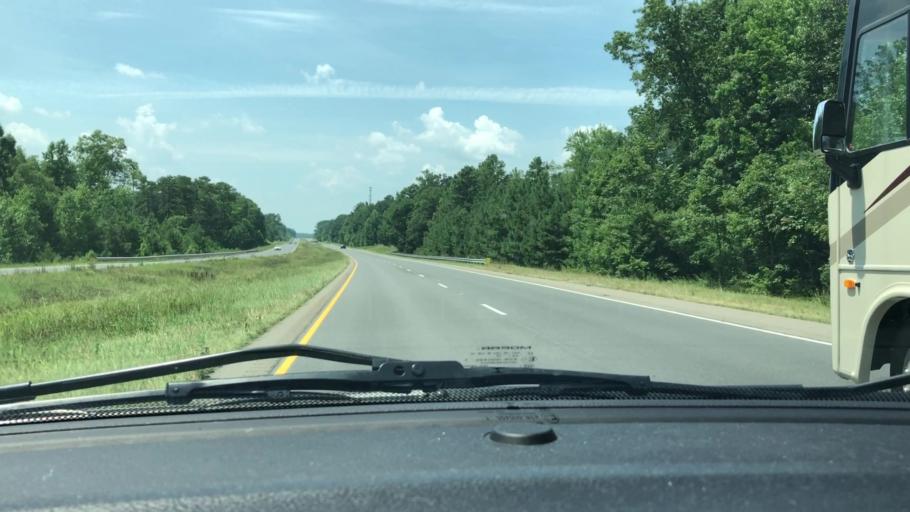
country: US
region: North Carolina
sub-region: Chatham County
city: Siler City
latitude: 35.6418
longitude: -79.3788
